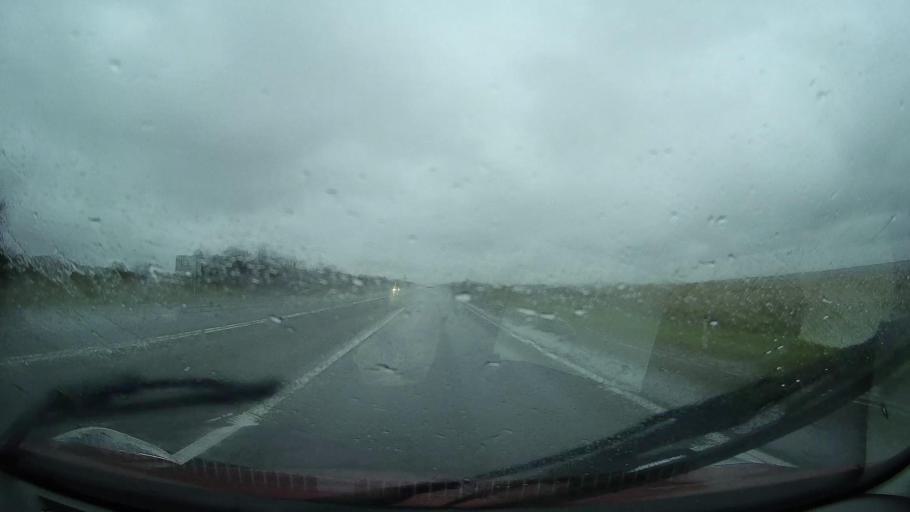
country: RU
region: Stavropol'skiy
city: Nevinnomyssk
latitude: 44.6321
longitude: 42.0198
